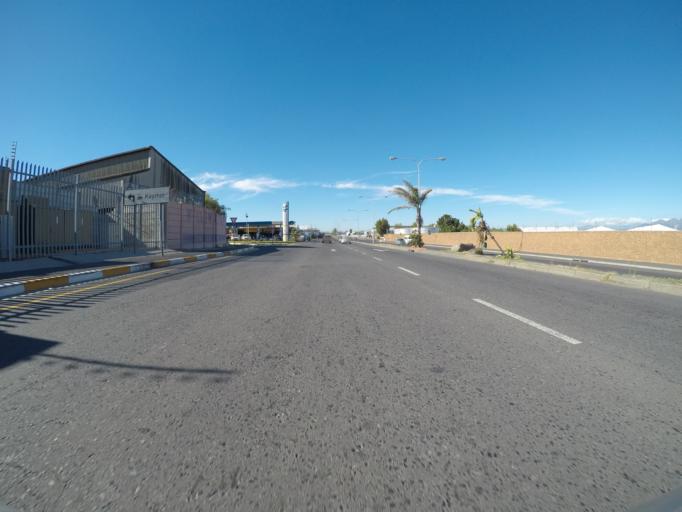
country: ZA
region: Western Cape
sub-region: City of Cape Town
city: Kraaifontein
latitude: -33.9045
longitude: 18.6680
